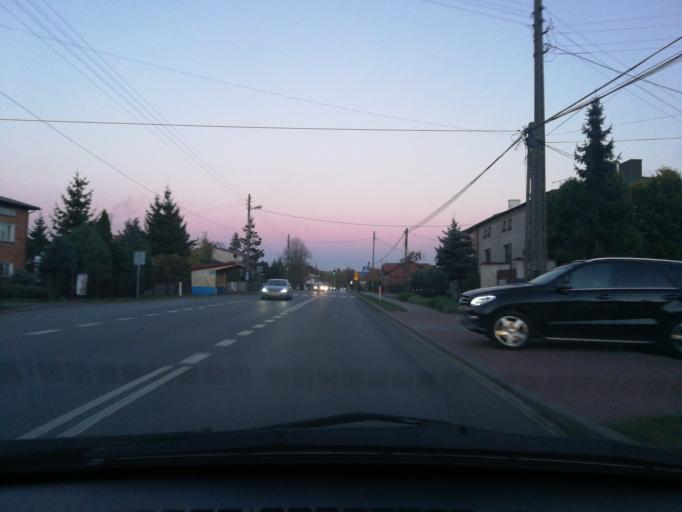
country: PL
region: Lodz Voivodeship
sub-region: Powiat brzezinski
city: Brzeziny
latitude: 51.8064
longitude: 19.6691
